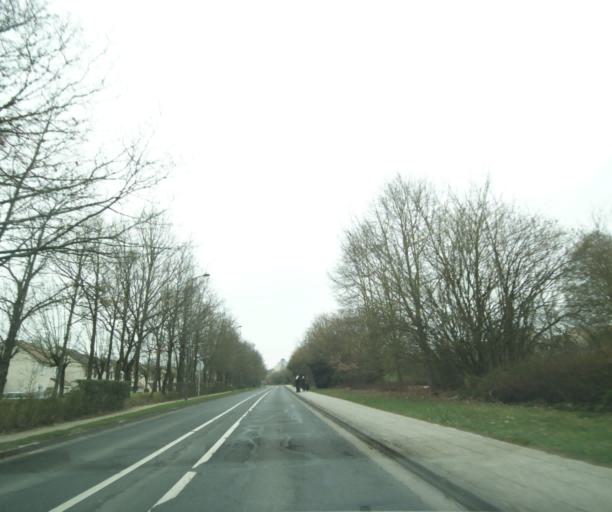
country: FR
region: Ile-de-France
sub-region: Departement du Val-d'Oise
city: Courdimanche
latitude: 49.0422
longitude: 2.0127
